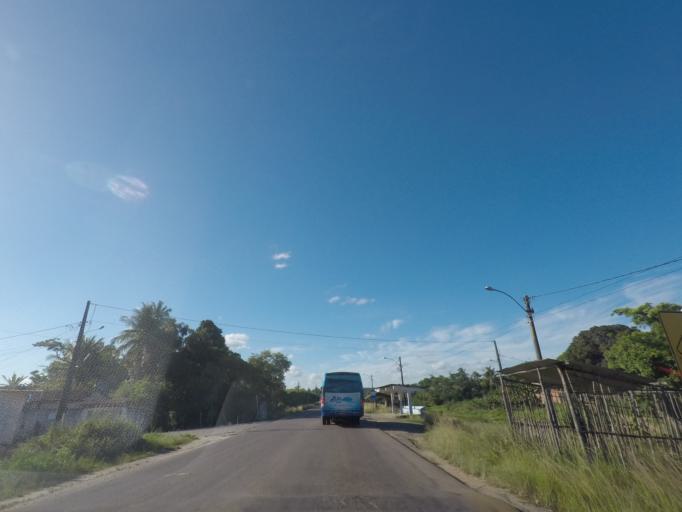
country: BR
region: Bahia
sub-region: Nazare
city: Nazare
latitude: -13.0786
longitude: -38.9978
